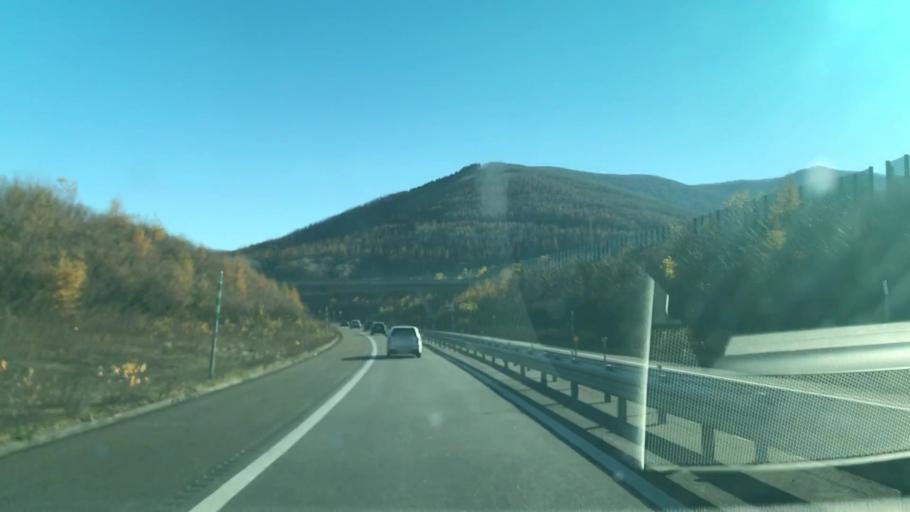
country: JP
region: Hokkaido
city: Otofuke
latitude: 43.0425
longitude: 142.7837
